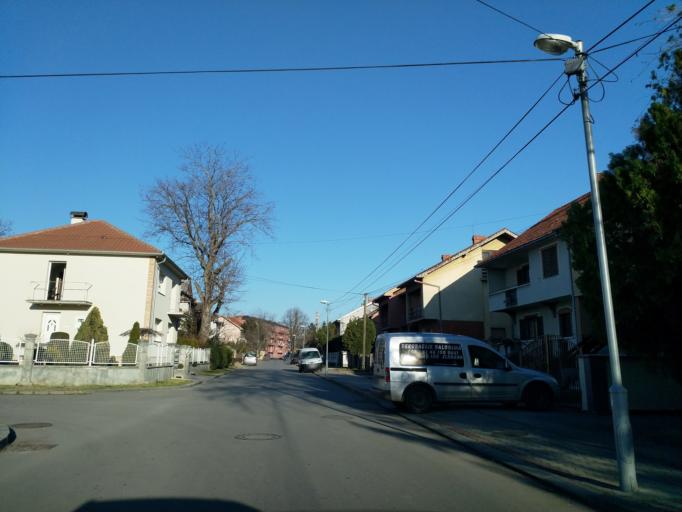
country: RS
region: Central Serbia
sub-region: Pomoravski Okrug
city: Paracin
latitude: 43.8646
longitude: 21.4182
